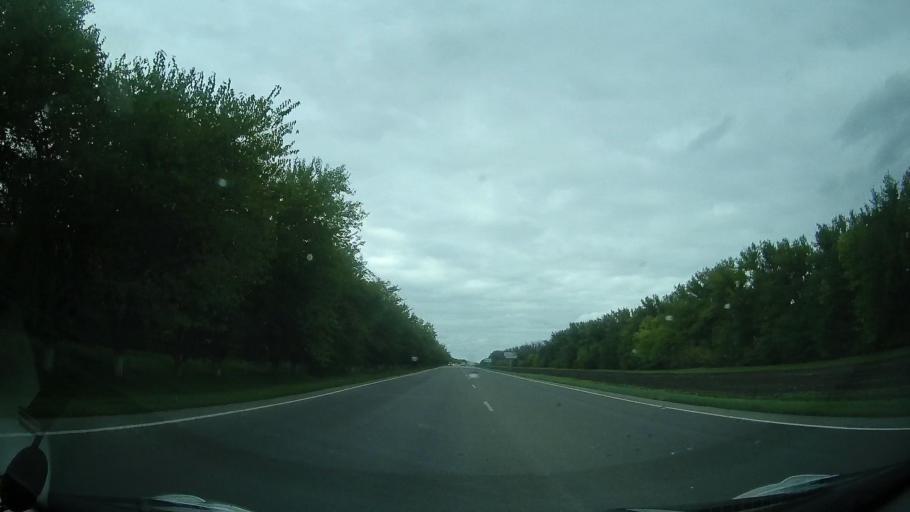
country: RU
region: Rostov
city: Yegorlykskaya
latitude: 46.6101
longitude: 40.6082
